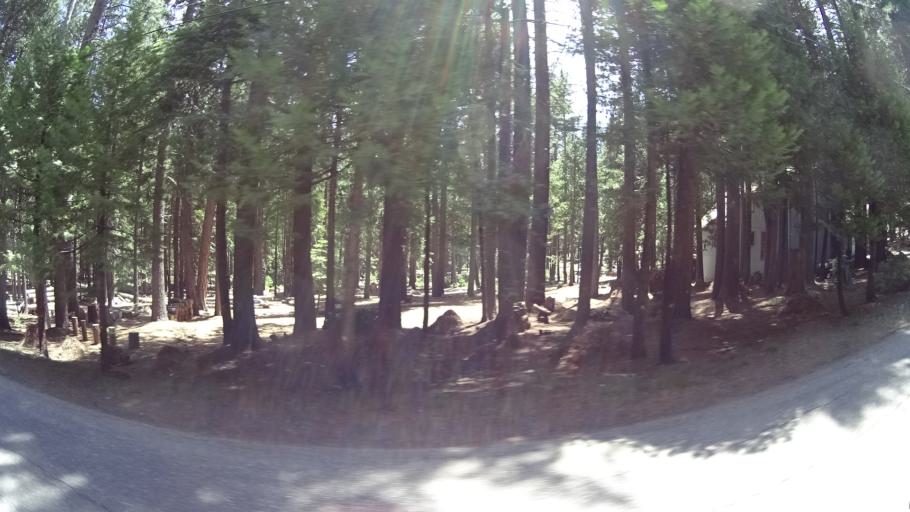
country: US
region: California
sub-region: Calaveras County
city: Arnold
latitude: 38.3060
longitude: -120.2579
